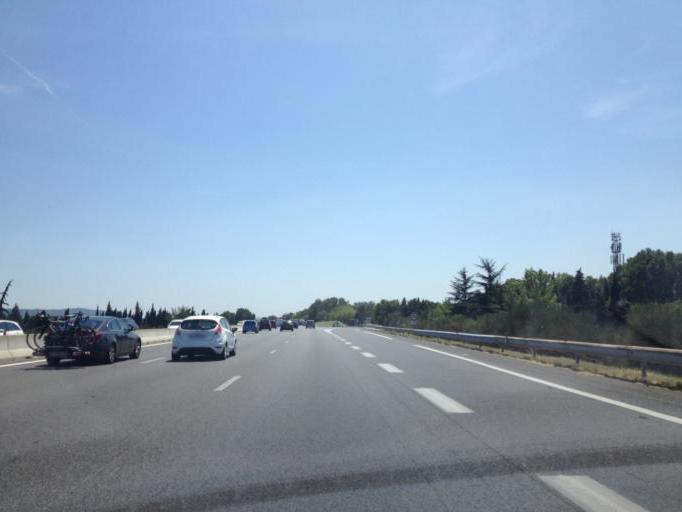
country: FR
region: Rhone-Alpes
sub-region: Departement de la Drome
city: La Garde-Adhemar
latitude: 44.4059
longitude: 4.7291
